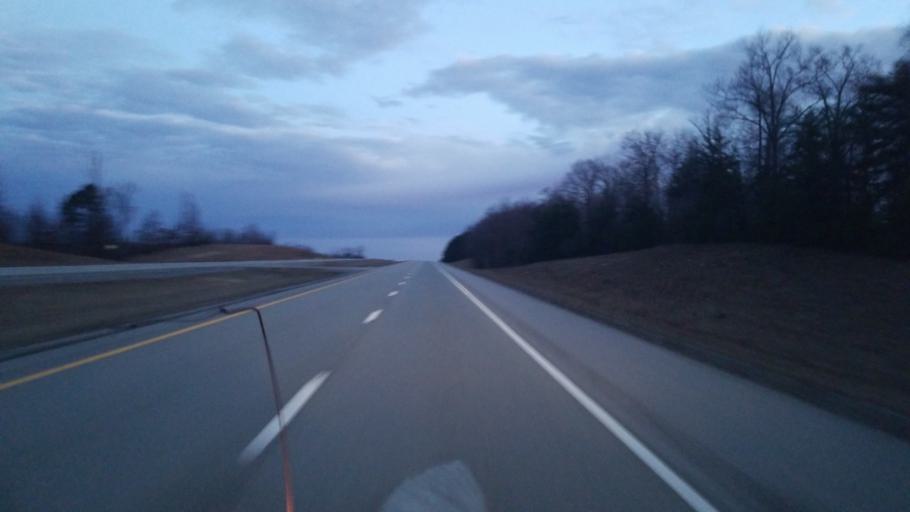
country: US
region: Tennessee
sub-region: Van Buren County
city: Spencer
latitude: 35.6562
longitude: -85.4738
